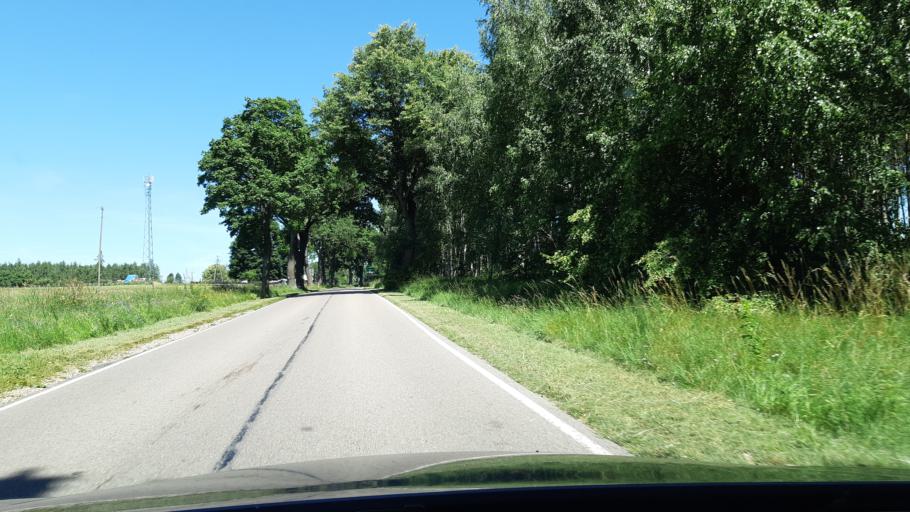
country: PL
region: Warmian-Masurian Voivodeship
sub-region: Powiat gizycki
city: Ryn
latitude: 53.8895
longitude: 21.6580
